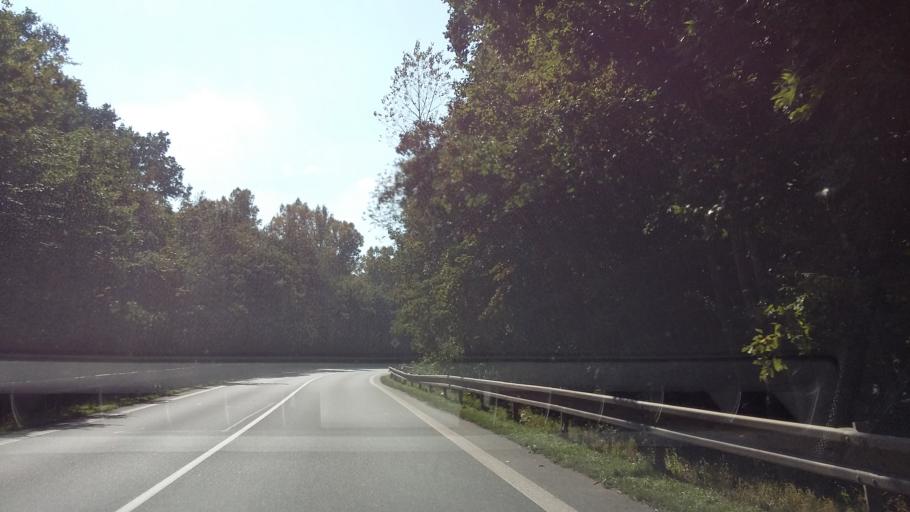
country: CZ
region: Central Bohemia
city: Libice nad Cidlinou
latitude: 50.1206
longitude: 15.1694
